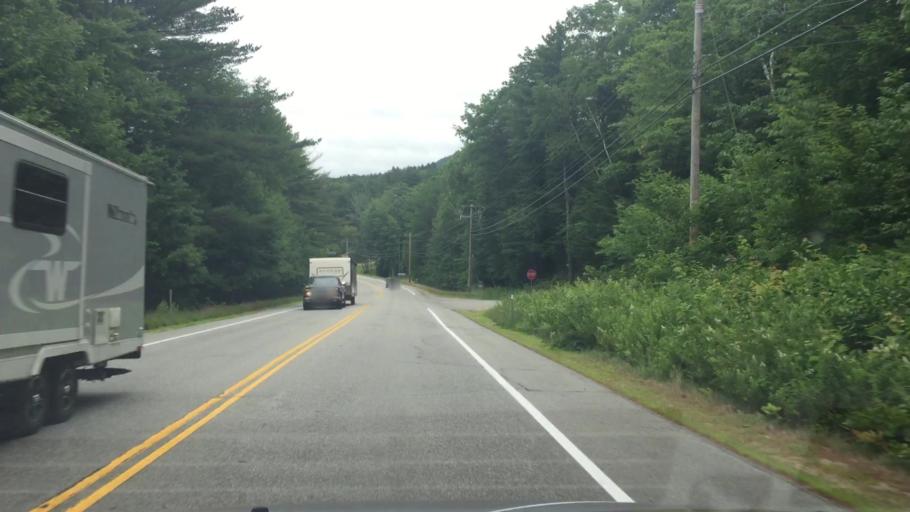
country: US
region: New Hampshire
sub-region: Carroll County
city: Sandwich
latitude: 43.8004
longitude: -71.3629
